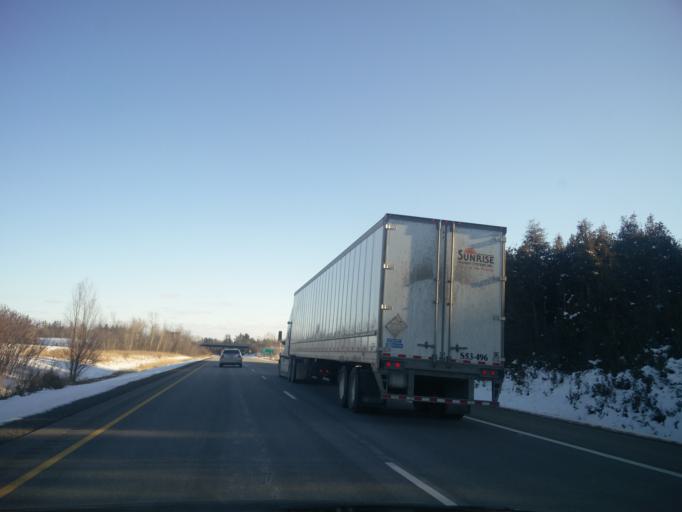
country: CA
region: Ontario
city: Prescott
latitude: 44.8386
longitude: -75.5317
